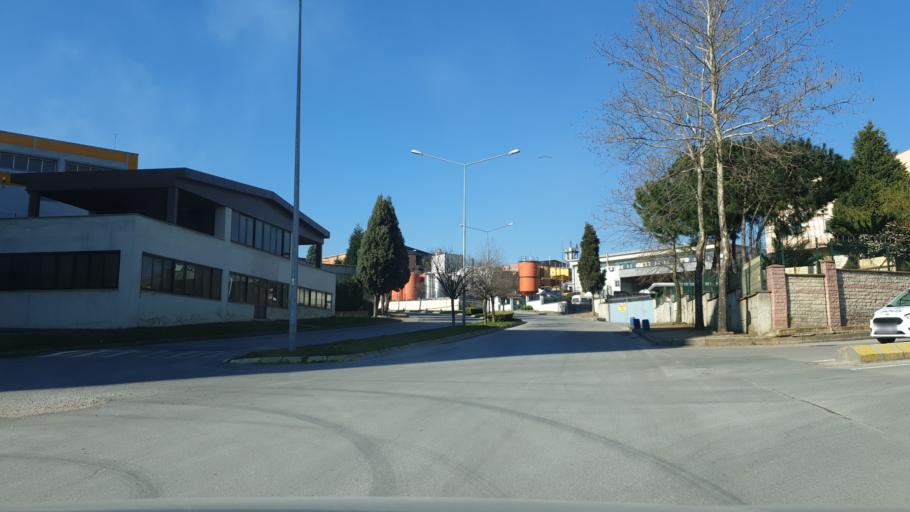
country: TR
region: Kocaeli
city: Balcik
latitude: 40.8790
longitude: 29.3717
